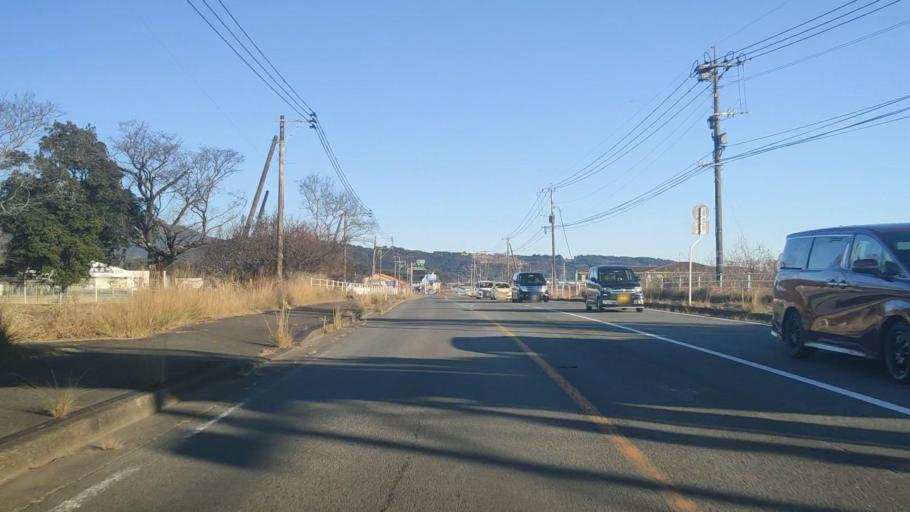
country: JP
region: Miyazaki
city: Takanabe
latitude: 32.2468
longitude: 131.5517
